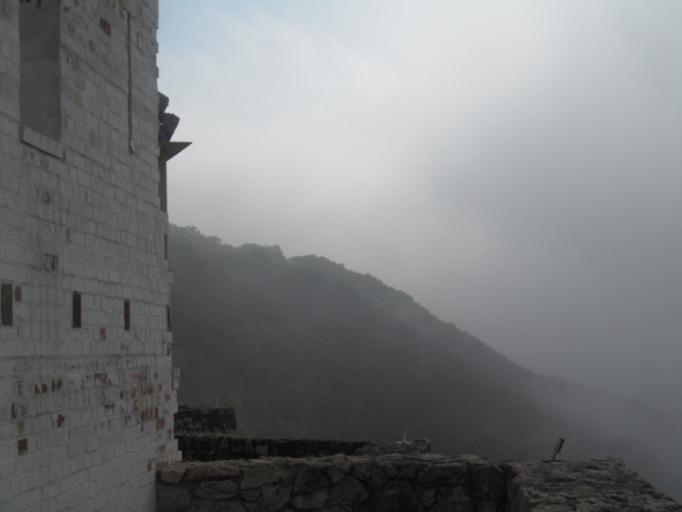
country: HU
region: Fejer
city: Bodajk
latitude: 47.3602
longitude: 18.2769
